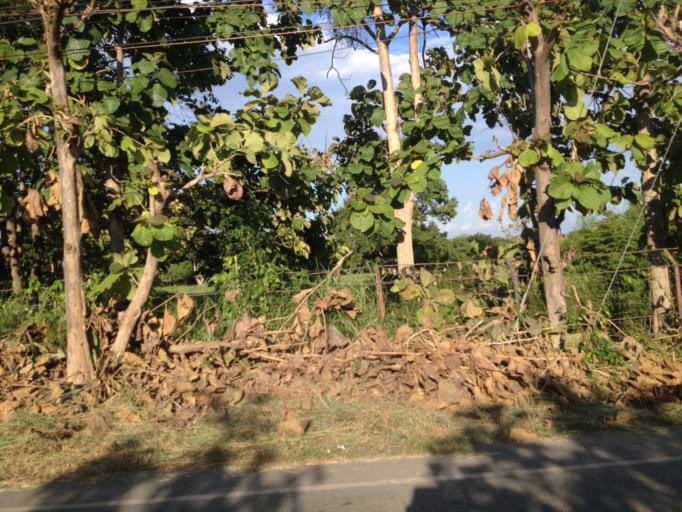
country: TH
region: Chiang Mai
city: Hang Dong
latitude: 18.7470
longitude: 98.9262
